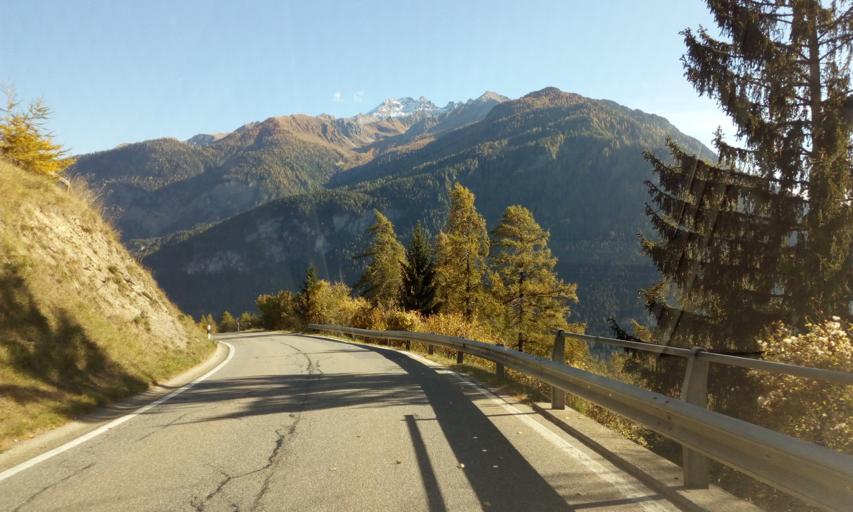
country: CH
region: Grisons
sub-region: Albula District
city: Tiefencastel
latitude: 46.6702
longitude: 9.5838
